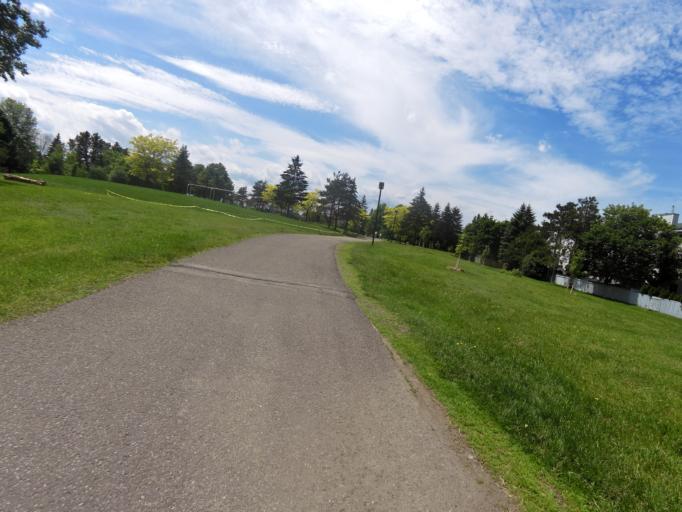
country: CA
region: Ontario
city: Ottawa
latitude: 45.3634
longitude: -75.6289
